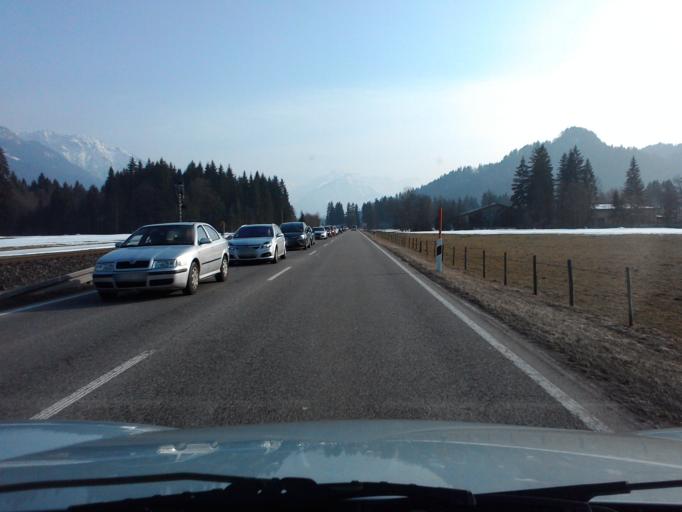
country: DE
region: Bavaria
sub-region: Swabia
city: Obermaiselstein
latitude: 47.4511
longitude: 10.2724
